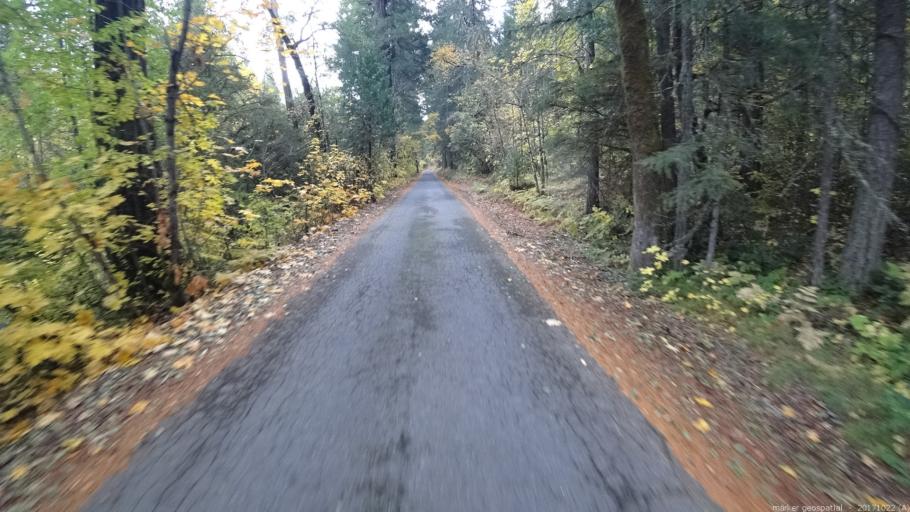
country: US
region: California
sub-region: Siskiyou County
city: Dunsmuir
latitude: 41.1696
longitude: -122.2808
